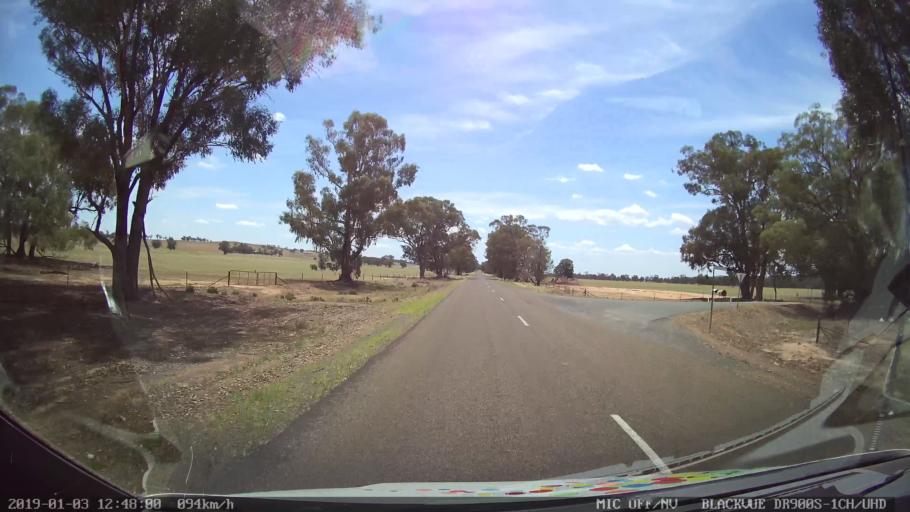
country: AU
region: New South Wales
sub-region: Weddin
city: Grenfell
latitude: -33.7198
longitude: 148.2468
